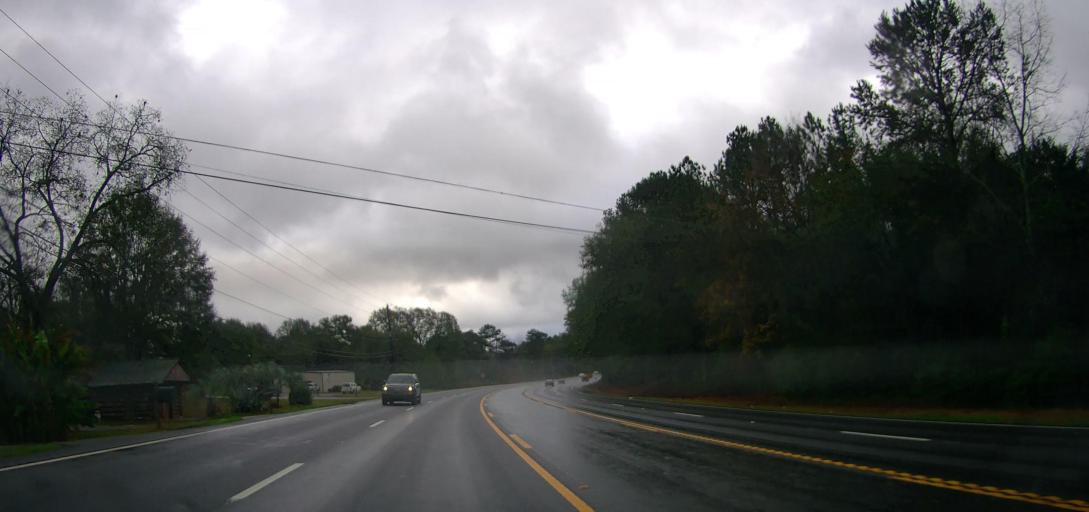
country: US
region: Georgia
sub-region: Clarke County
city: Country Club Estates
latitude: 34.0161
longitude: -83.3891
